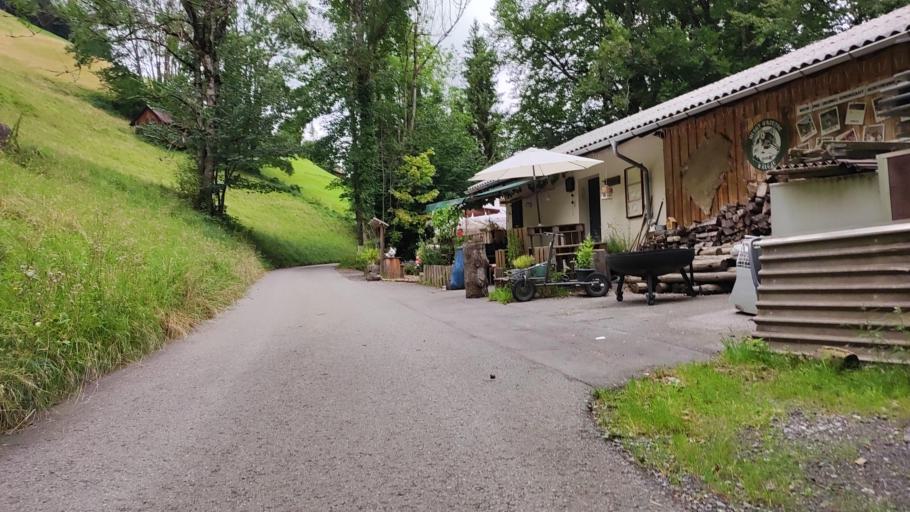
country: AT
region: Vorarlberg
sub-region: Politischer Bezirk Feldkirch
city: Feldkirch
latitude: 47.2061
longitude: 9.6104
